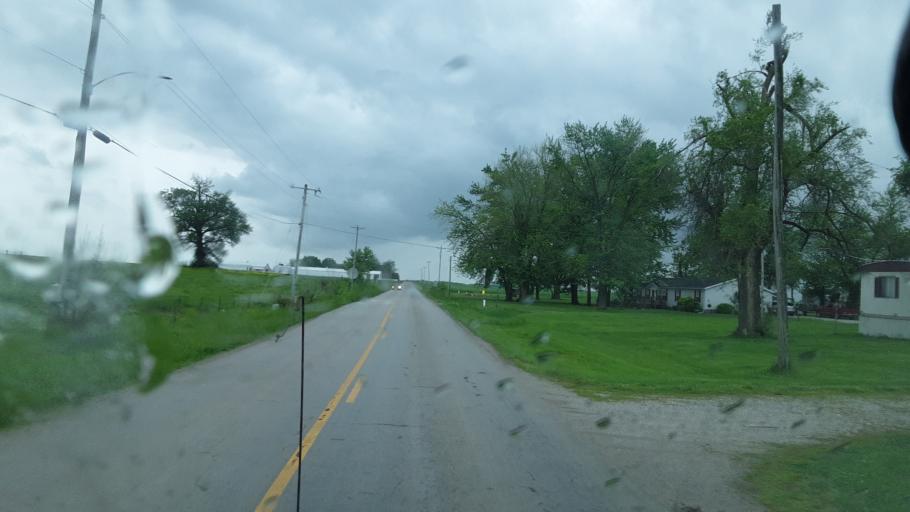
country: US
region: Missouri
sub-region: Monroe County
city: Paris
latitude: 39.4690
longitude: -92.2126
